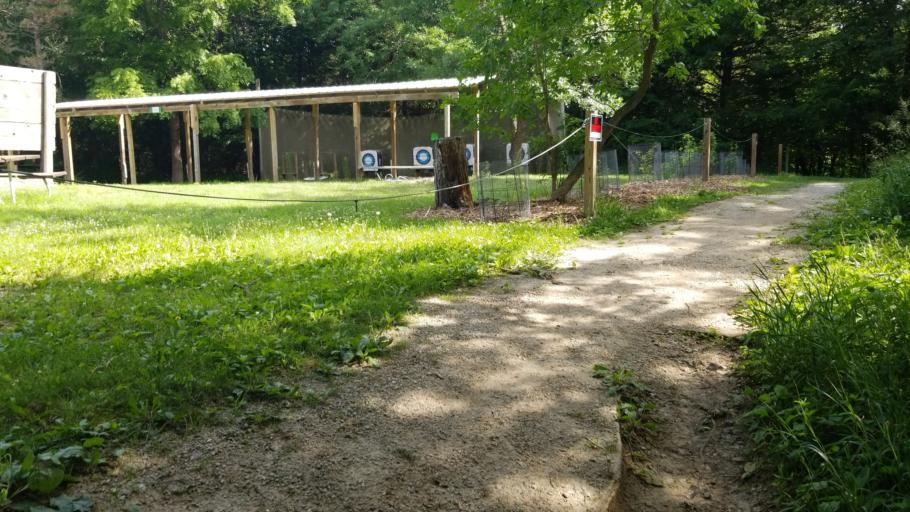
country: US
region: Nebraska
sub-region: Cass County
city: Louisville
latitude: 41.0252
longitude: -96.2508
